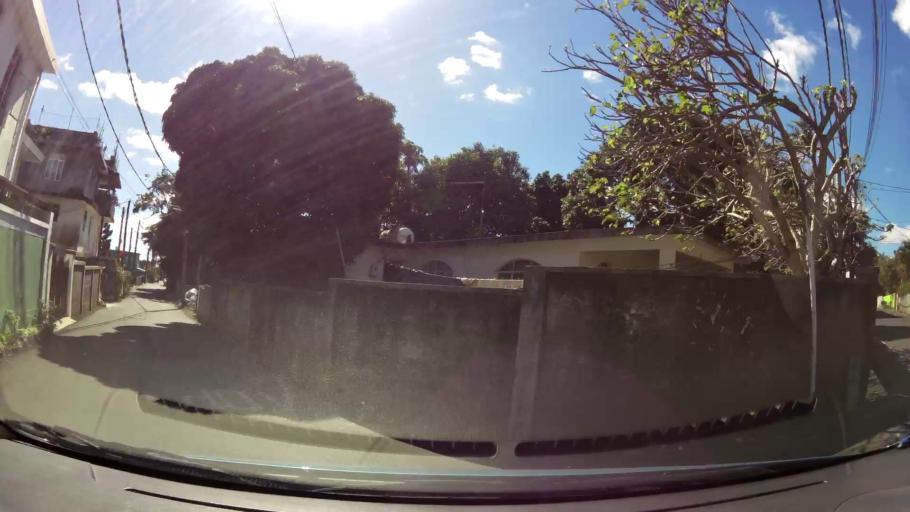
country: MU
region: Plaines Wilhems
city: Vacoas
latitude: -20.2977
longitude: 57.4862
